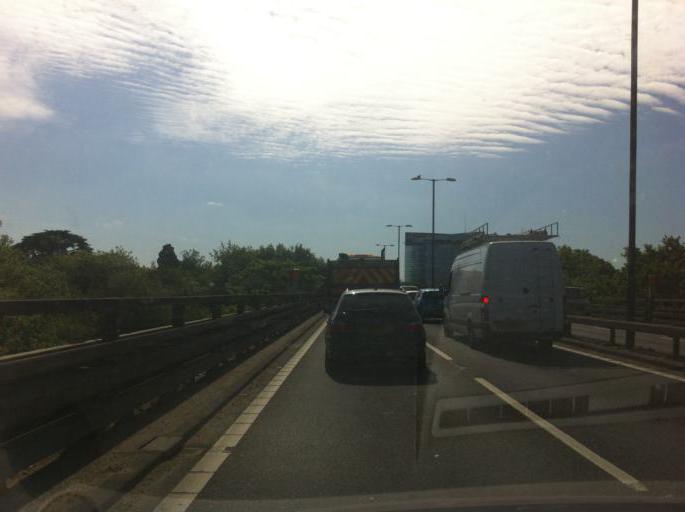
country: GB
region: England
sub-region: Greater London
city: Brentford
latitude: 51.4921
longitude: -0.3233
